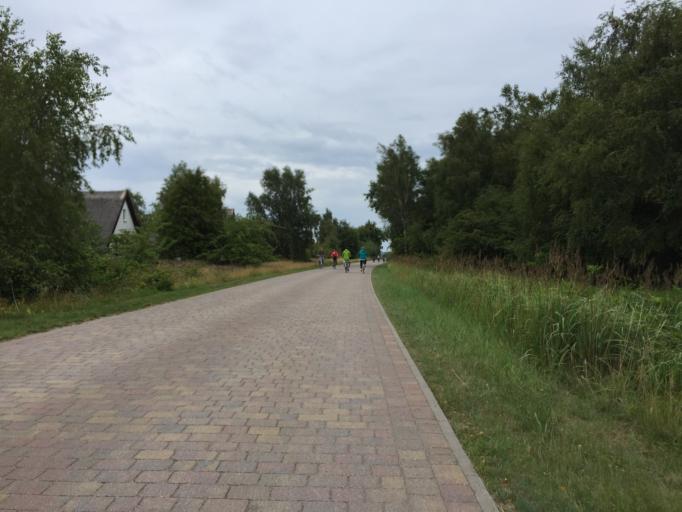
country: DE
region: Mecklenburg-Vorpommern
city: Hiddensee
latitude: 54.5473
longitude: 13.1057
